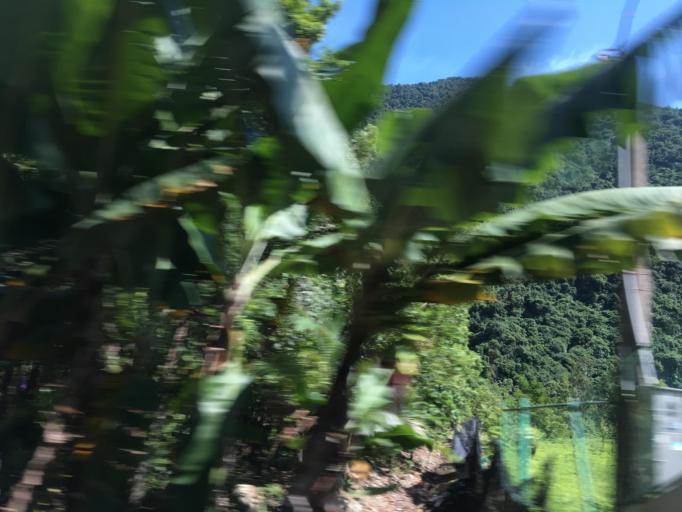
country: TW
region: Taiwan
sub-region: Yilan
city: Yilan
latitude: 24.4386
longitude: 121.7521
